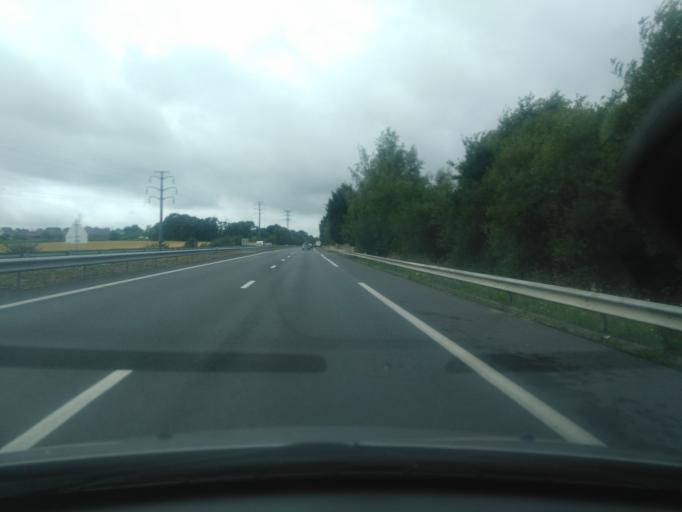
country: FR
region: Brittany
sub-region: Departement des Cotes-d'Armor
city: Quevert
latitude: 48.4614
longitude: -2.0712
